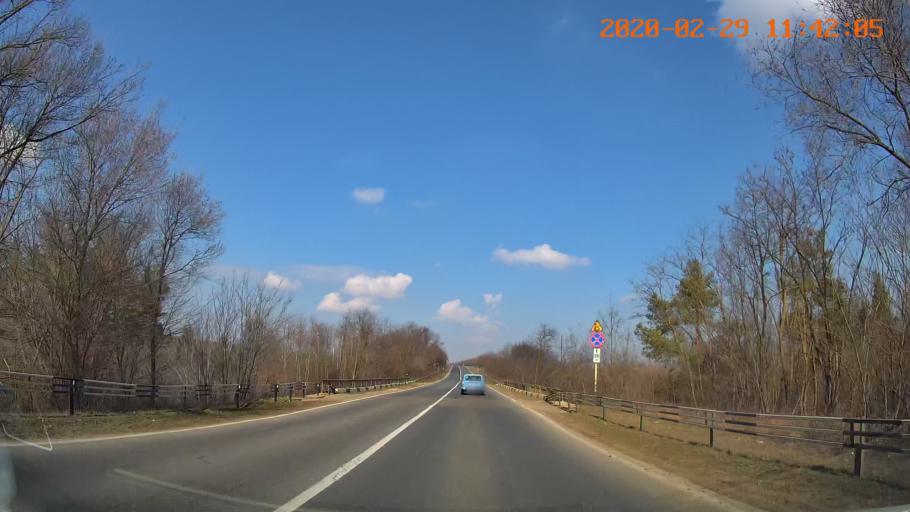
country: MD
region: Rezina
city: Saharna
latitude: 47.6796
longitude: 29.0143
